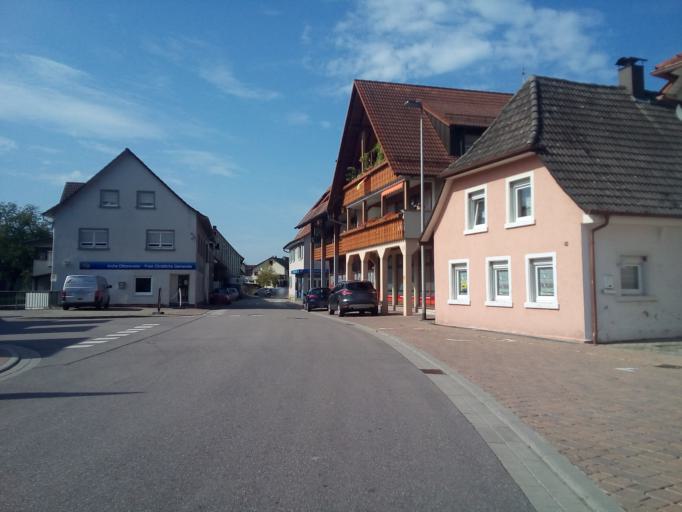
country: DE
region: Baden-Wuerttemberg
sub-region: Karlsruhe Region
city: Ottersweier
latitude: 48.6684
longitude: 8.1098
